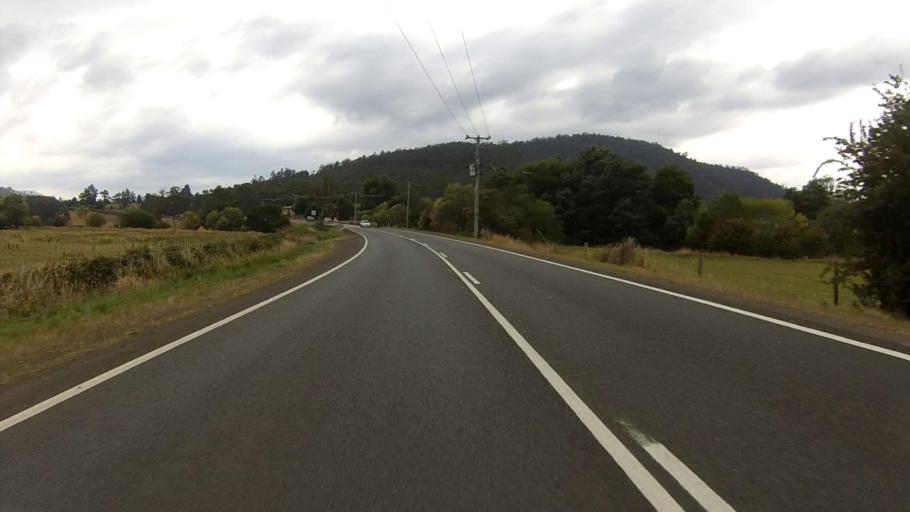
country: AU
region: Tasmania
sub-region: Huon Valley
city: Franklin
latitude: -43.0710
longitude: 147.0399
